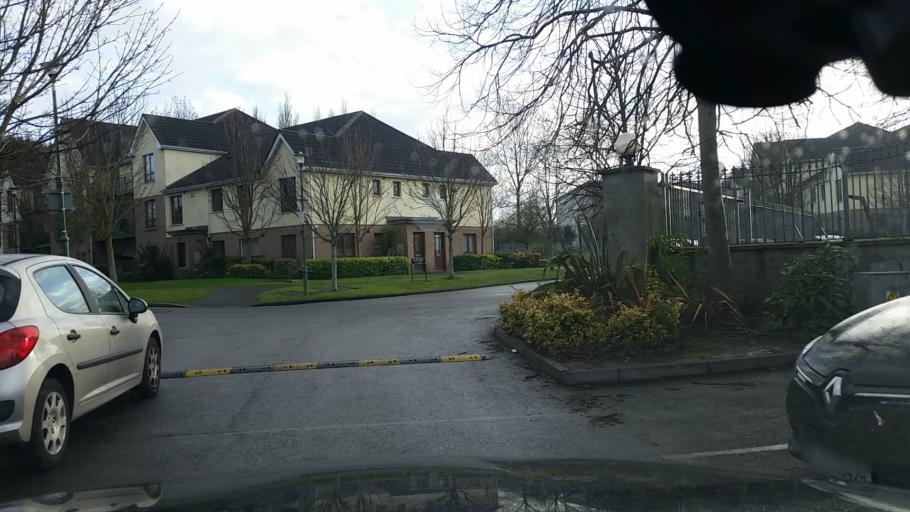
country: IE
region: Leinster
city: Beaumont
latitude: 53.3988
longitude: -6.2283
